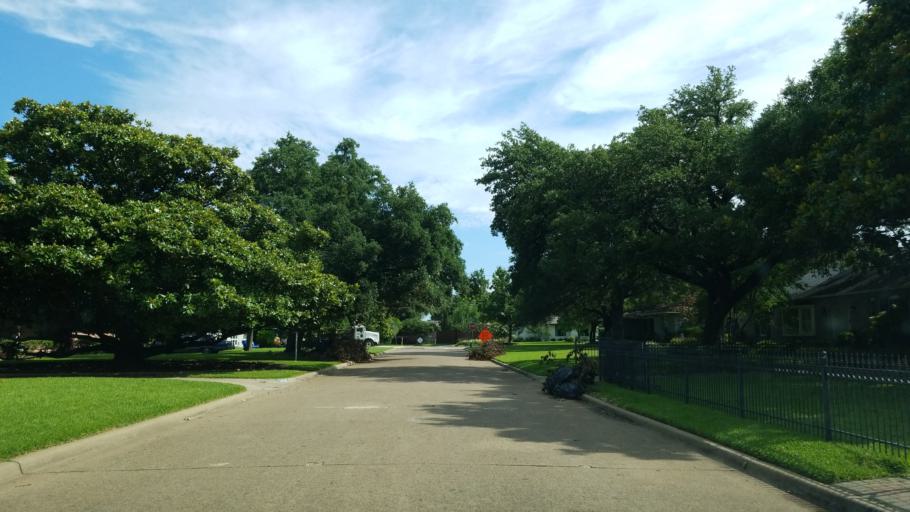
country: US
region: Texas
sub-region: Dallas County
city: Farmers Branch
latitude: 32.9014
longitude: -96.8434
